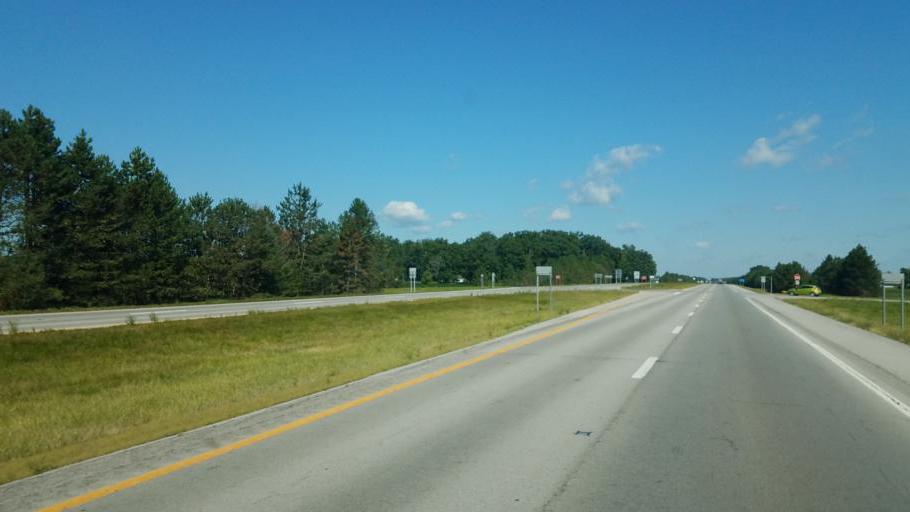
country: US
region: Ohio
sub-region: Wyandot County
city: Carey
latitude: 40.8898
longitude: -83.3386
